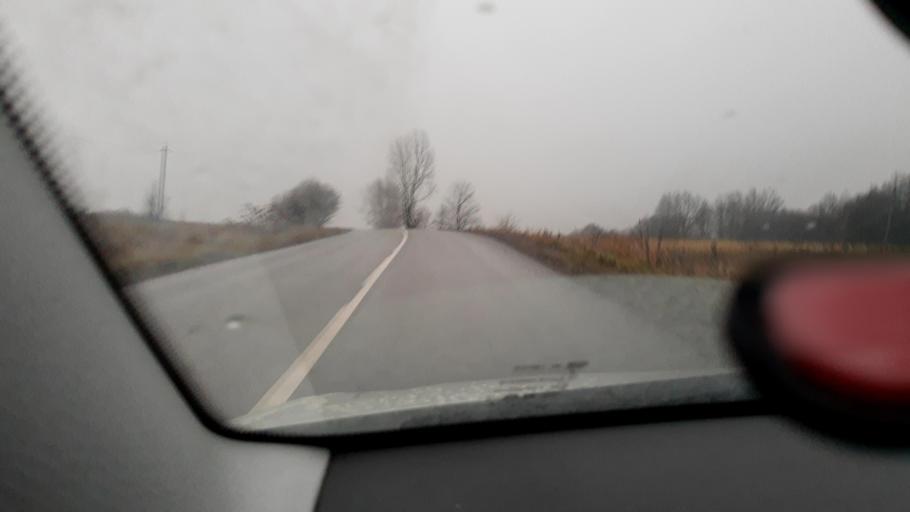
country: RU
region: Bashkortostan
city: Iglino
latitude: 54.8996
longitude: 56.2561
